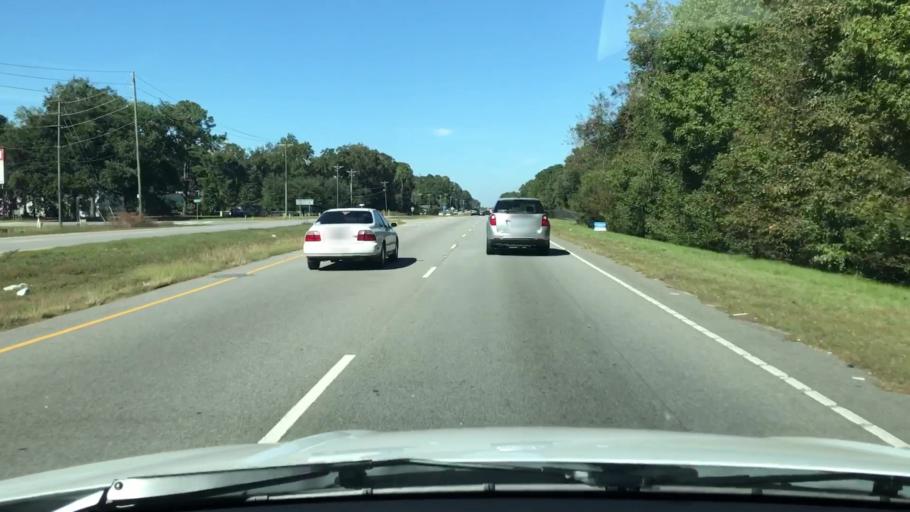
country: US
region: South Carolina
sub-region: Beaufort County
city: Burton
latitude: 32.4798
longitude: -80.7388
